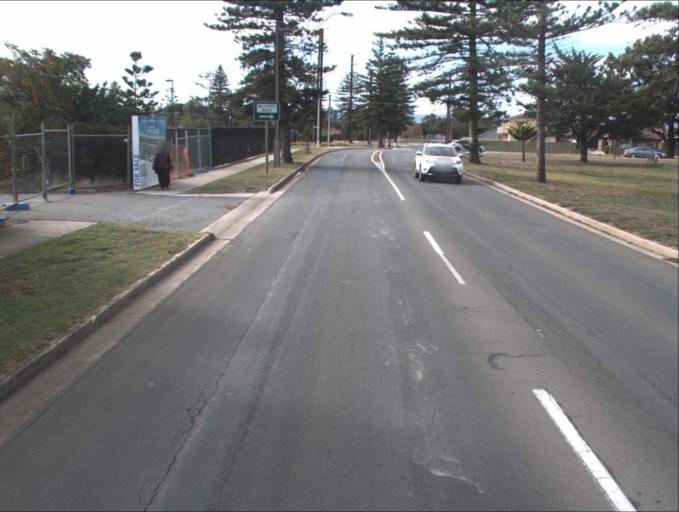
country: AU
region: South Australia
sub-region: Port Adelaide Enfield
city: Birkenhead
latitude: -34.8122
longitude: 138.4934
